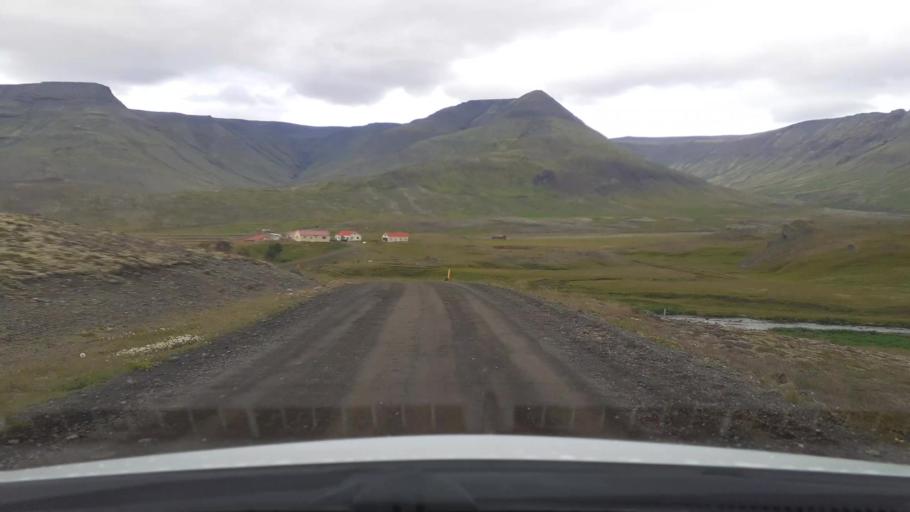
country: IS
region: Capital Region
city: Mosfellsbaer
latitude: 64.2055
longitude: -21.5629
